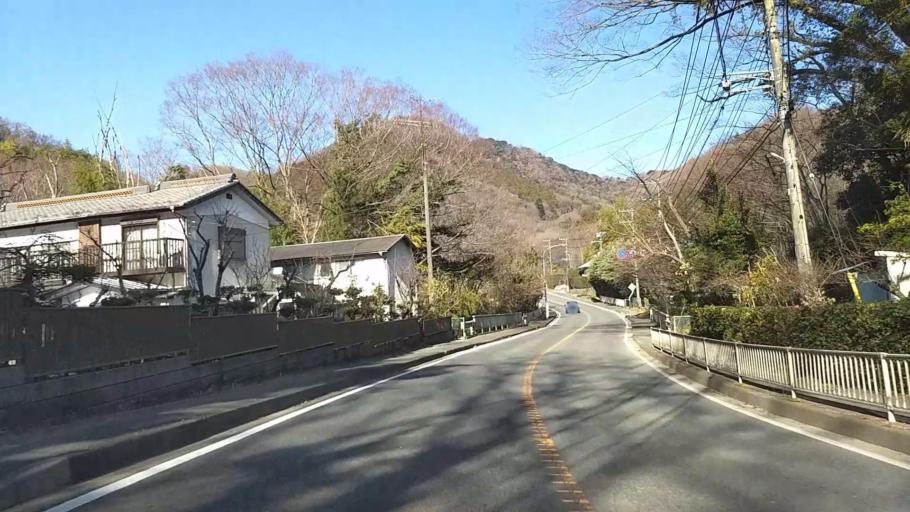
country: JP
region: Kanagawa
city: Atsugi
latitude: 35.4814
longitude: 139.3040
